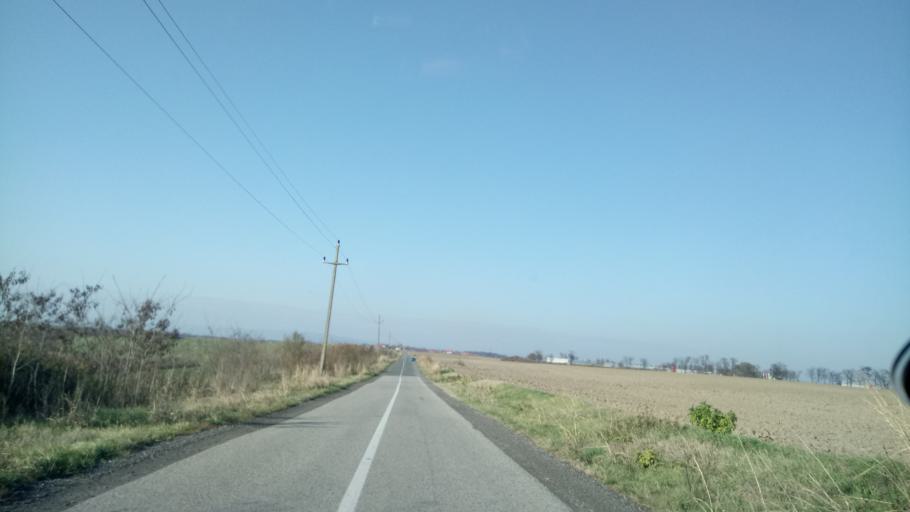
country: RS
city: Ljukovo
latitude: 45.0338
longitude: 20.0443
